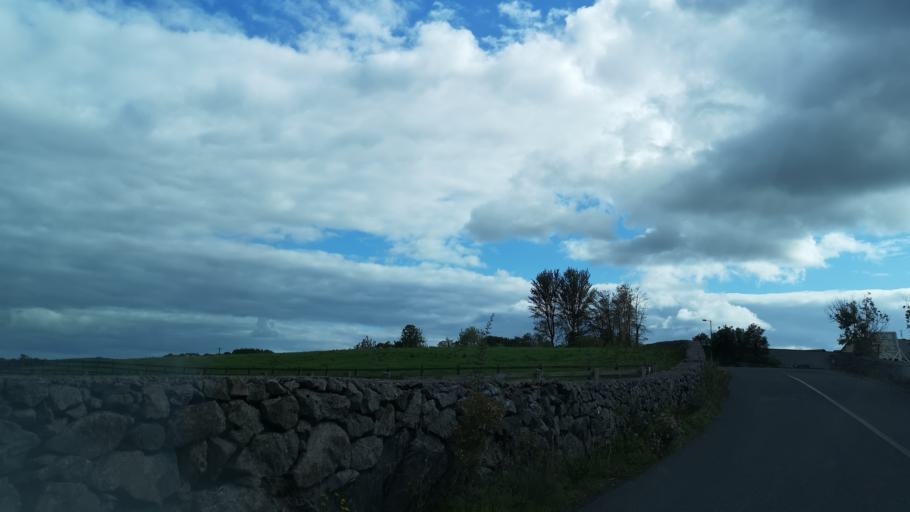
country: IE
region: Connaught
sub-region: County Galway
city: Moycullen
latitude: 53.3440
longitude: -9.1757
